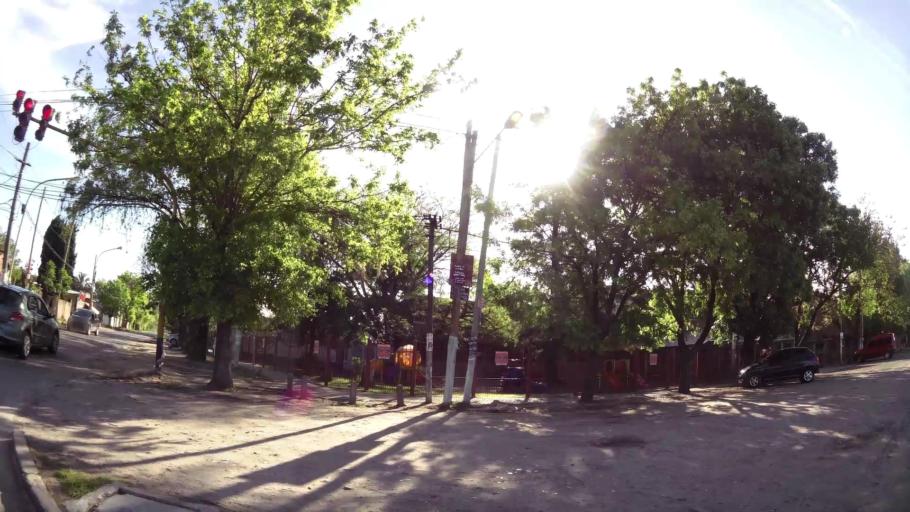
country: AR
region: Buenos Aires
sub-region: Partido de Quilmes
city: Quilmes
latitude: -34.7957
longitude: -58.2134
